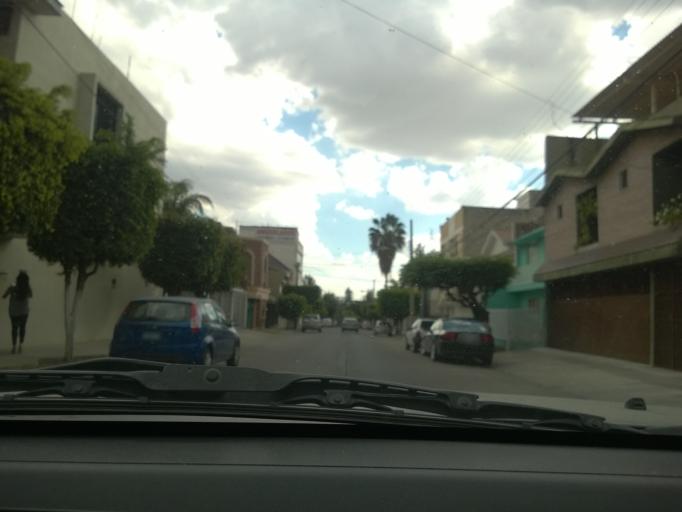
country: MX
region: Guanajuato
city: Leon
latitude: 21.1421
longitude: -101.6923
